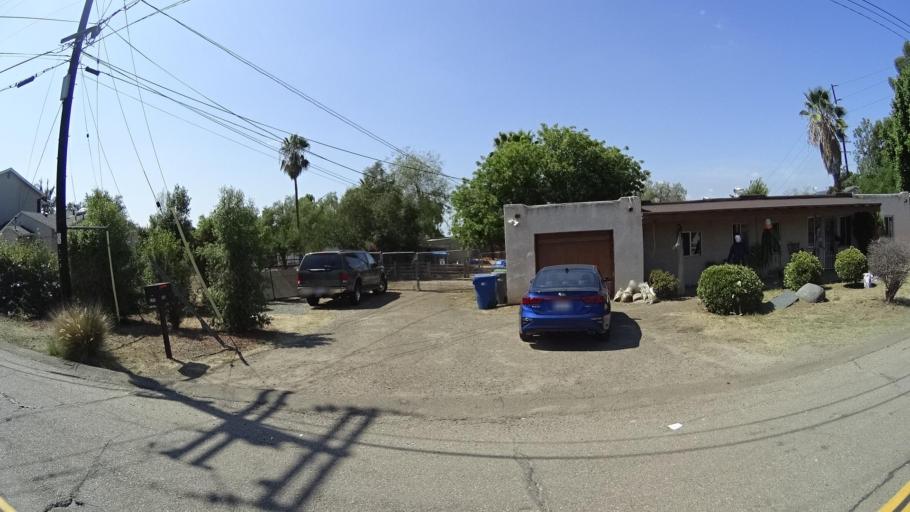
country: US
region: California
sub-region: San Diego County
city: Spring Valley
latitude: 32.7403
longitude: -116.9922
